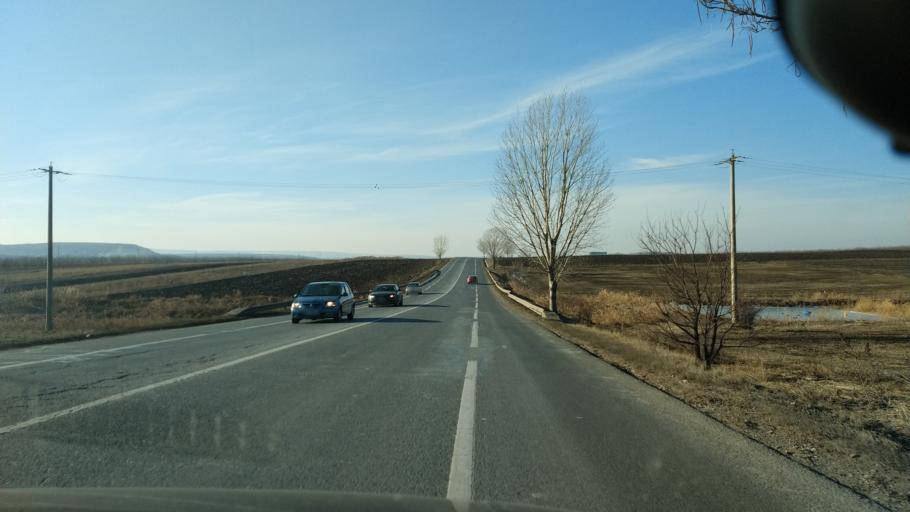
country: RO
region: Iasi
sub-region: Comuna Baltati
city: Baltati
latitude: 47.2206
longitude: 27.1007
